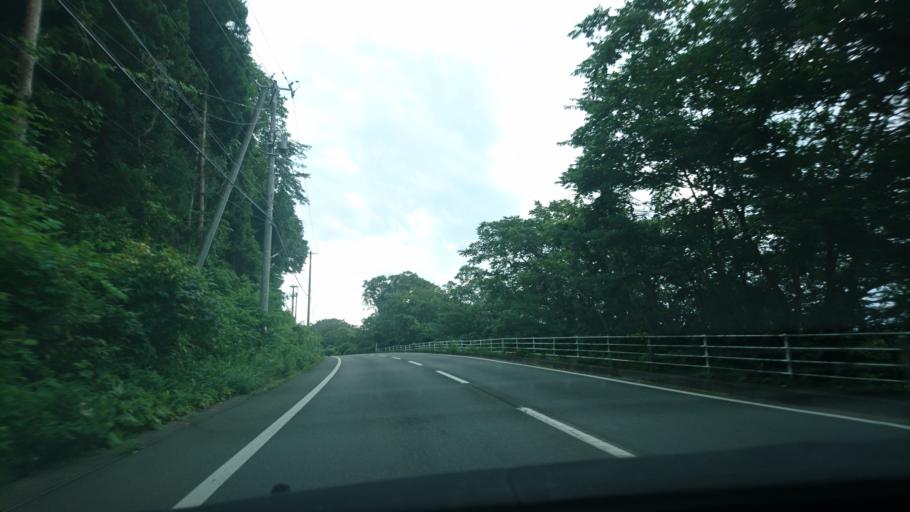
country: JP
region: Iwate
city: Kitakami
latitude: 39.2641
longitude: 141.1245
